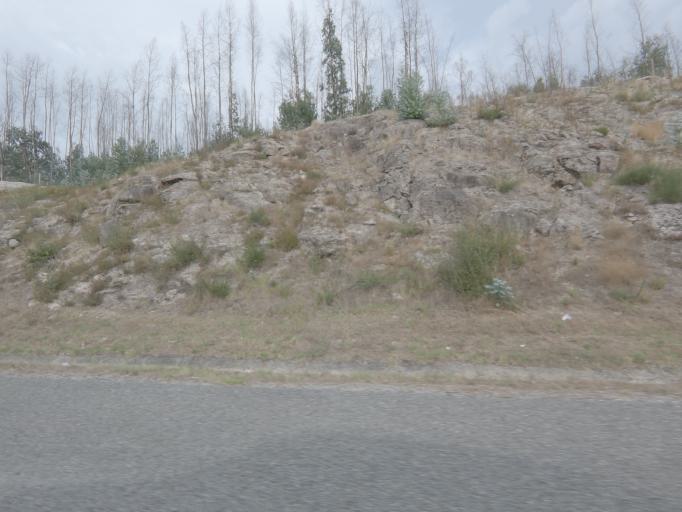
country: PT
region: Viseu
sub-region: Santa Comba Dao
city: Santa Comba Dao
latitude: 40.4477
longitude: -8.1060
